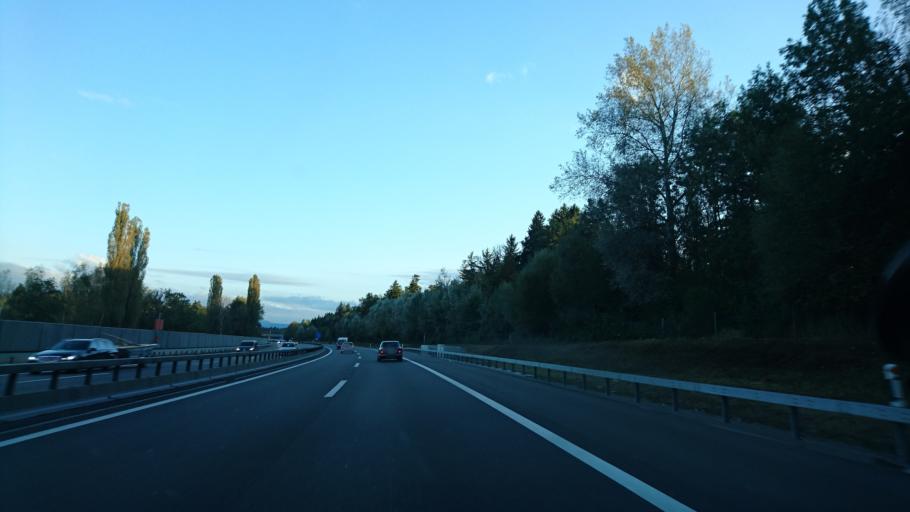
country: CH
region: Bern
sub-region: Bern-Mittelland District
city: Rubigen
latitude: 46.8956
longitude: 7.5342
